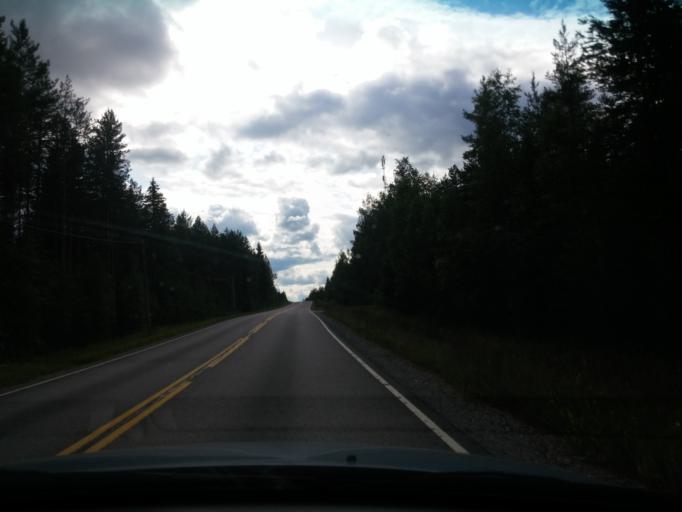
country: FI
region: Central Finland
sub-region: Saarijaervi-Viitasaari
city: Pylkoenmaeki
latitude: 62.6320
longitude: 24.8050
